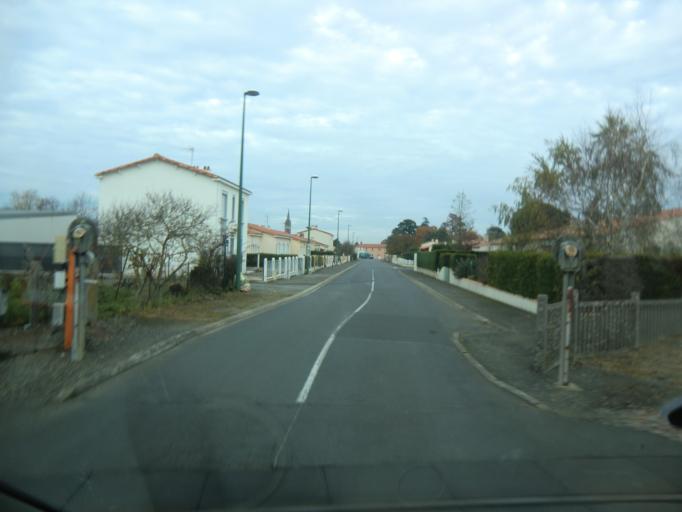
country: FR
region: Pays de la Loire
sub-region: Departement de la Vendee
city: Cugand
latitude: 47.0591
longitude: -1.2578
